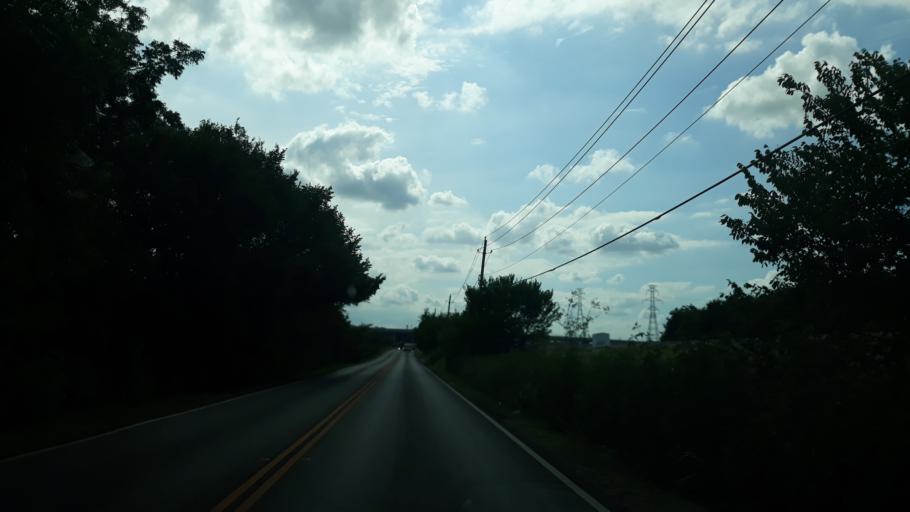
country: US
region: Texas
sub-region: Dallas County
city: Irving
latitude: 32.8158
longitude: -97.0114
